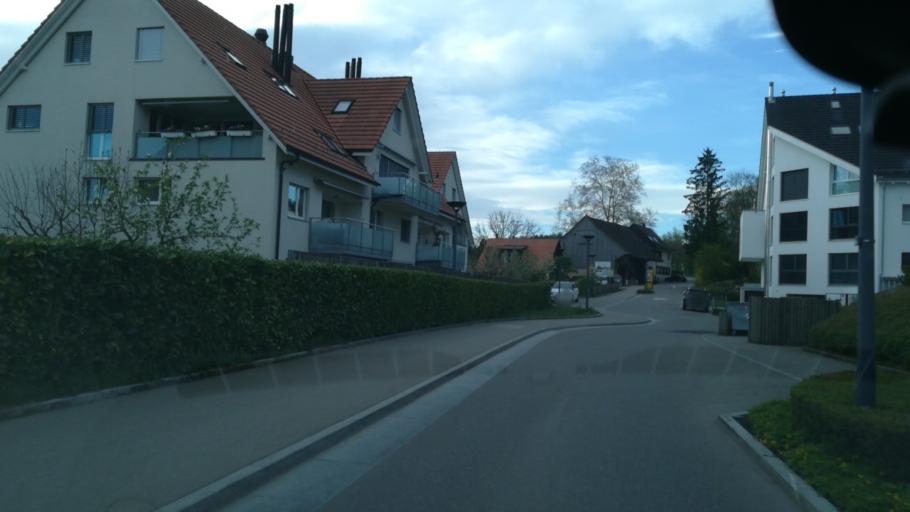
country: CH
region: Zurich
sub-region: Bezirk Uster
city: Gockhausen
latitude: 47.3766
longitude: 8.6070
